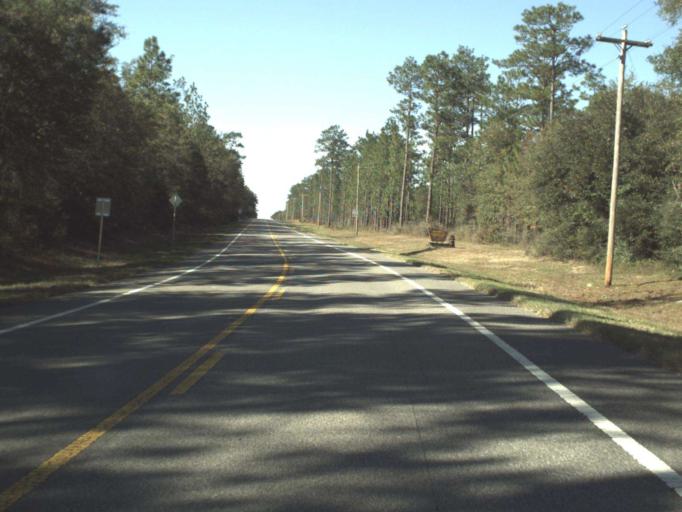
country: US
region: Florida
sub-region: Okaloosa County
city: Crestview
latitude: 30.8420
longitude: -86.7373
